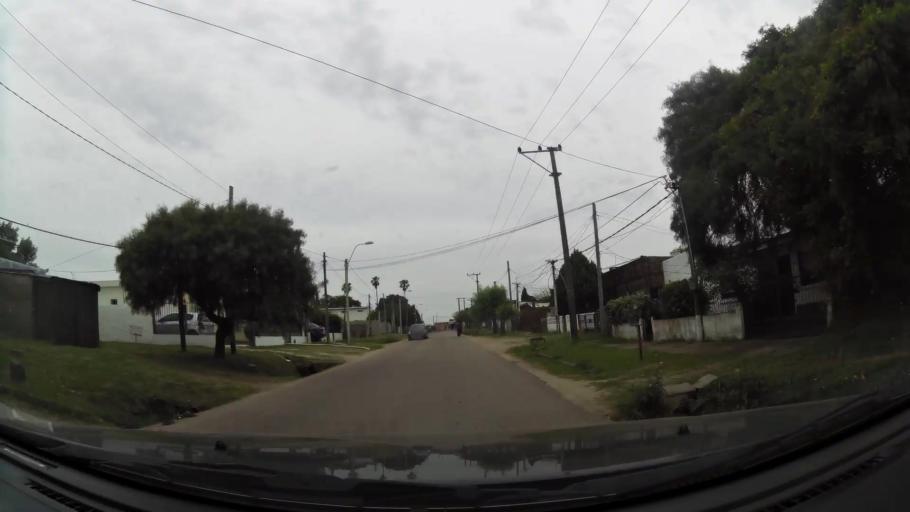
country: UY
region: Canelones
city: Las Piedras
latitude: -34.7204
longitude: -56.2052
